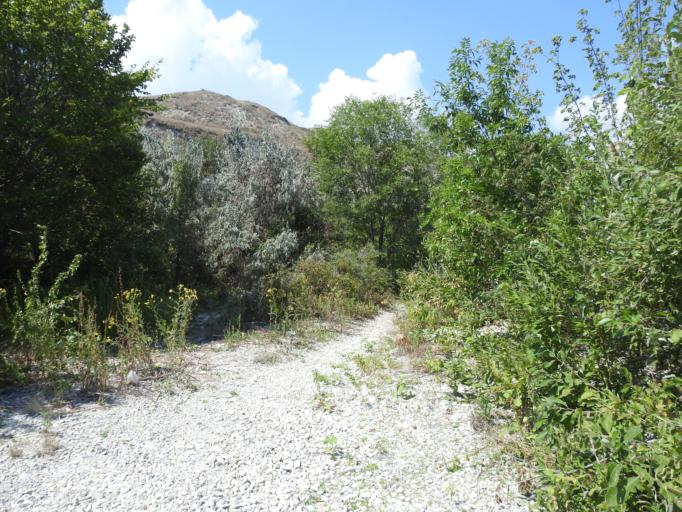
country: RU
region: Saratov
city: Kamenskiy
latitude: 50.5926
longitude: 45.6938
